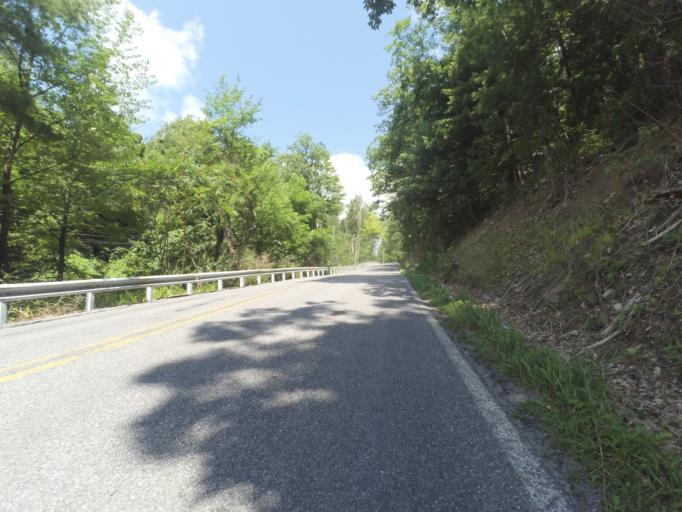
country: US
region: Pennsylvania
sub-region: Centre County
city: Stormstown
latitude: 40.7823
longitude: -78.0471
